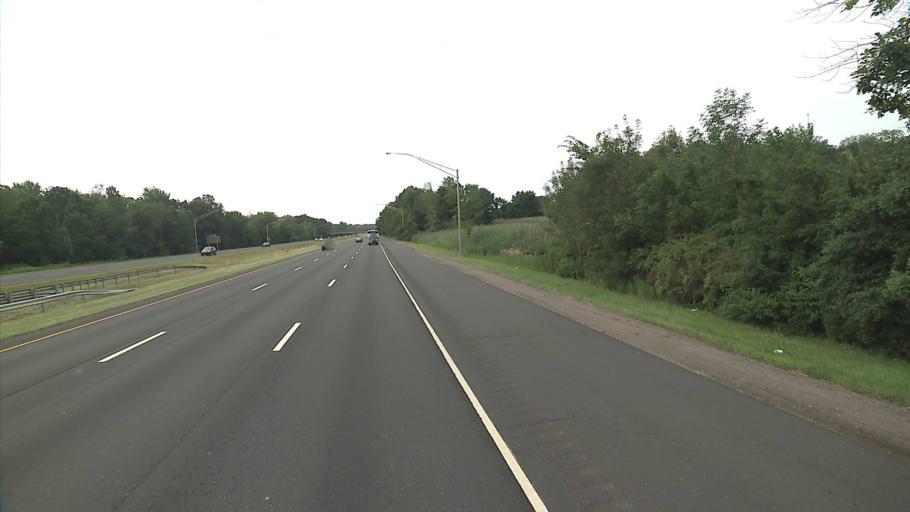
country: US
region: Connecticut
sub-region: Hartford County
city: Farmington
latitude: 41.7115
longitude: -72.8001
